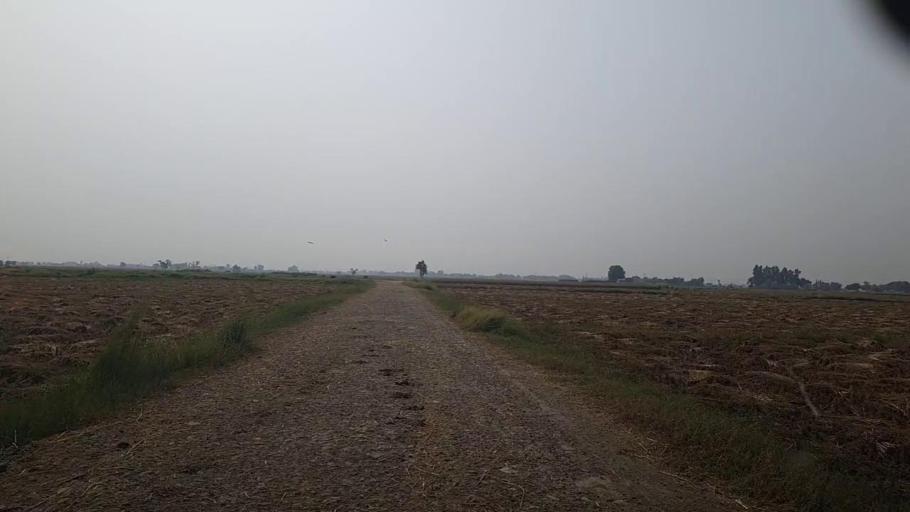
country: PK
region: Sindh
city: Kashmor
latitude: 28.3814
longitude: 69.4302
